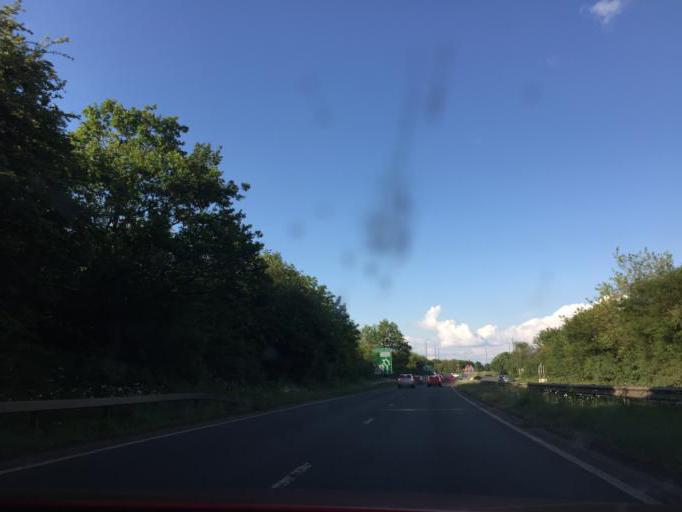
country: GB
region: England
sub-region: Warwickshire
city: Bedworth
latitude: 52.4962
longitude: -1.4767
